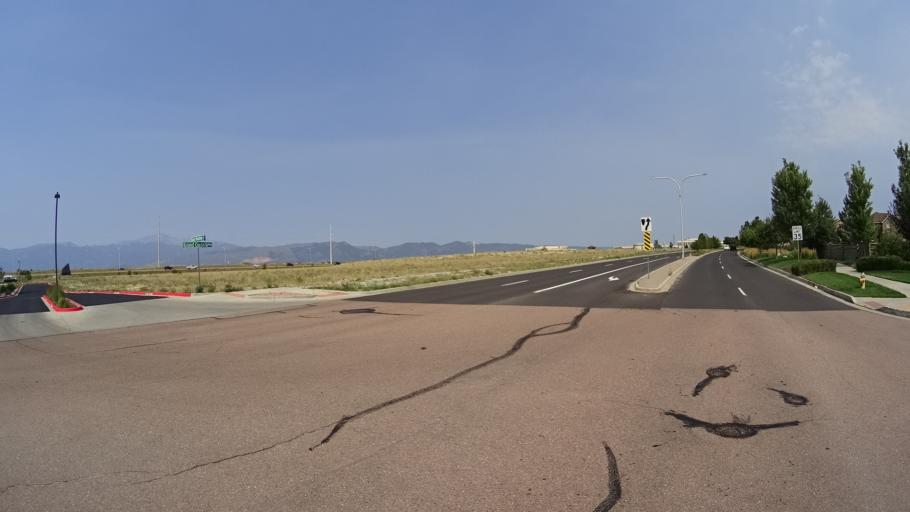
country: US
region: Colorado
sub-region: El Paso County
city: Black Forest
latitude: 38.9646
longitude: -104.7344
